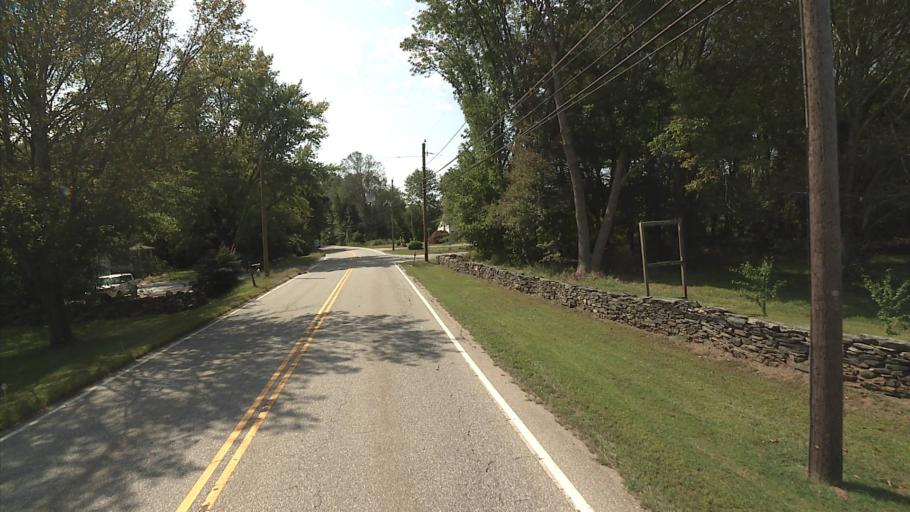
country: US
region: Connecticut
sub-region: Windham County
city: Plainfield Village
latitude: 41.6656
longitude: -71.9729
